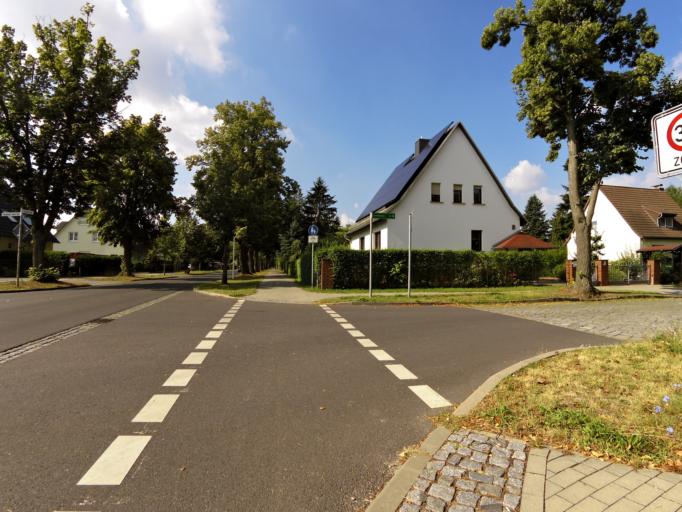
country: DE
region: Berlin
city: Lichtenrade
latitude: 52.3582
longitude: 13.4212
